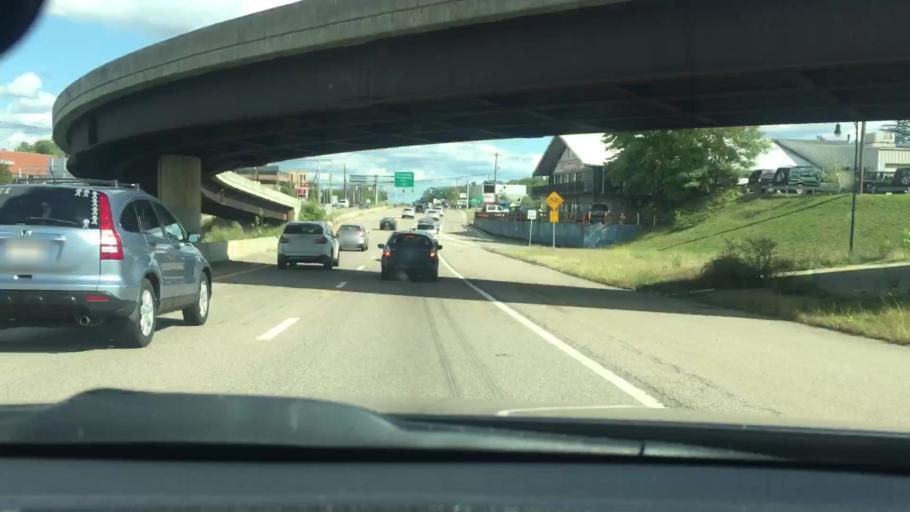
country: US
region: Massachusetts
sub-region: Worcester County
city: Southborough
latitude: 42.2949
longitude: -71.4983
